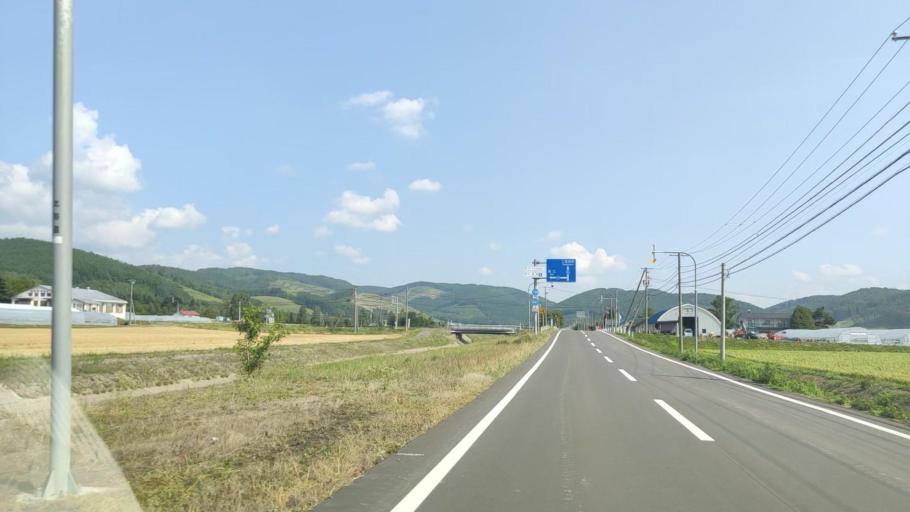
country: JP
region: Hokkaido
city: Shimo-furano
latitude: 43.4048
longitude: 142.3953
